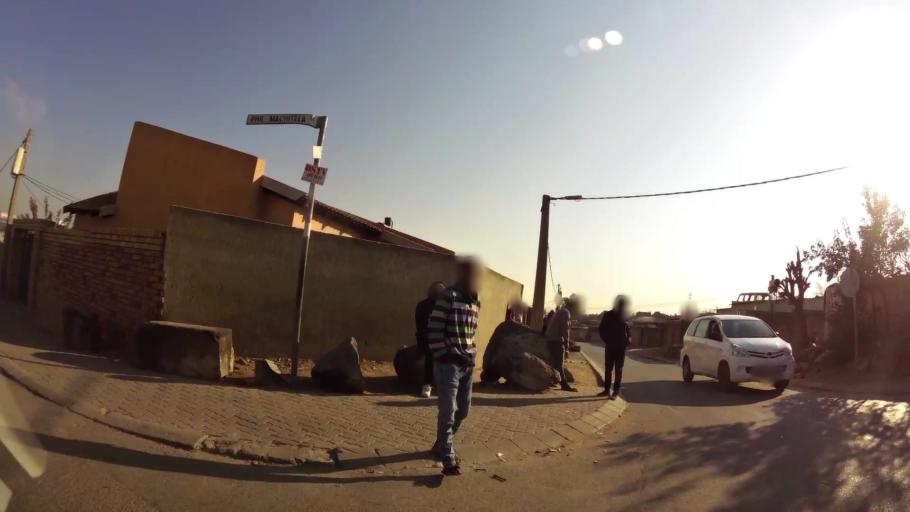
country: ZA
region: Gauteng
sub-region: City of Johannesburg Metropolitan Municipality
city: Modderfontein
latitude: -26.0910
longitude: 28.1120
